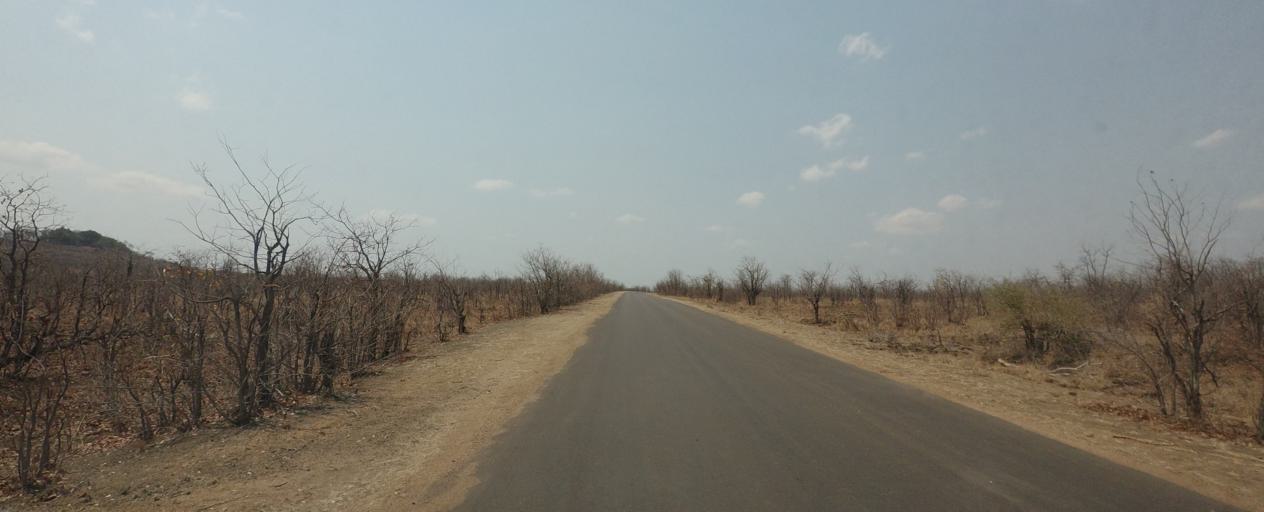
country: ZA
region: Limpopo
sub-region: Mopani District Municipality
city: Phalaborwa
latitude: -23.5207
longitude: 31.4014
